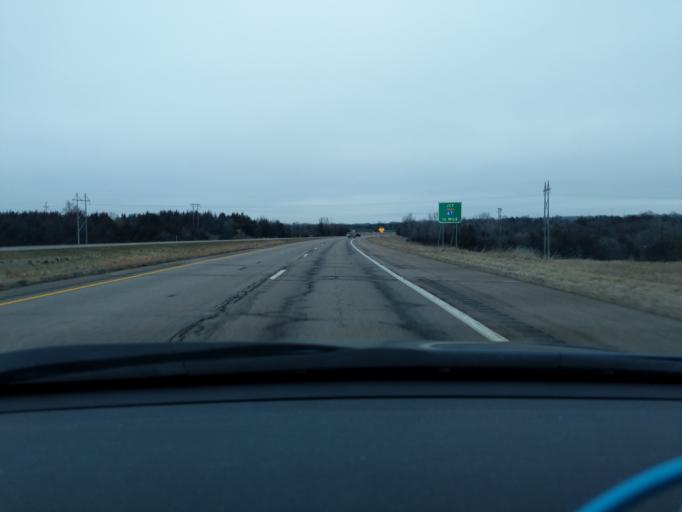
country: US
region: Minnesota
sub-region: Yellow Medicine County
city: Granite Falls
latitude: 44.7952
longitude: -95.5481
